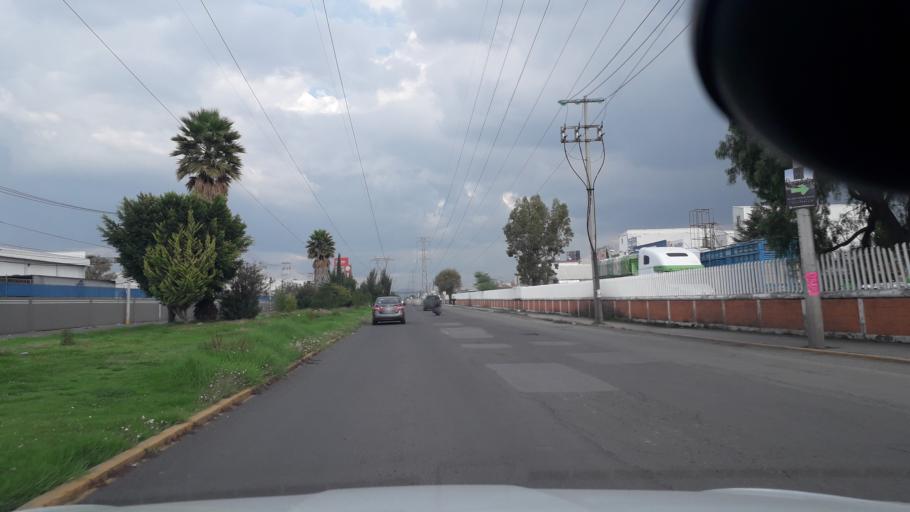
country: MX
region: Mexico
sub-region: Tultitlan
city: Fuentes del Valle
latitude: 19.6403
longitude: -99.1393
